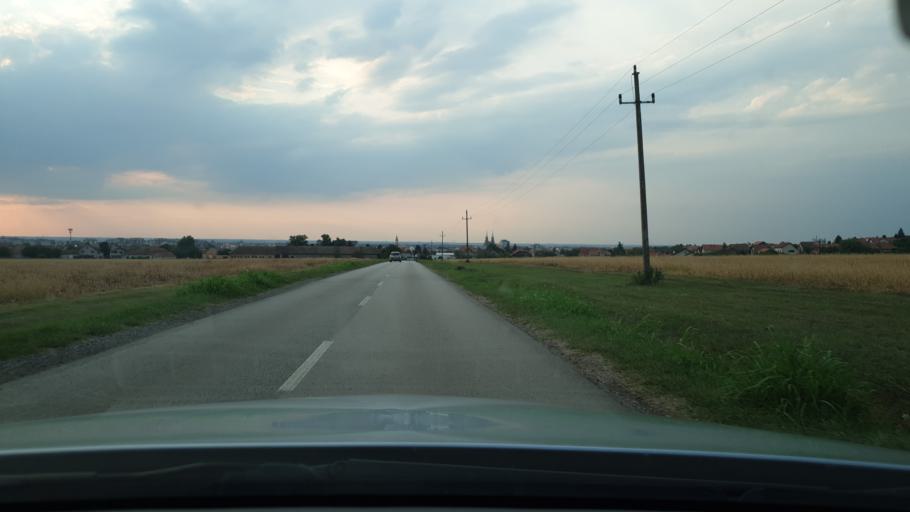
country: RS
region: Autonomna Pokrajina Vojvodina
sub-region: Juznobanatski Okrug
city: Vrsac
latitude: 45.1069
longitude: 21.3154
